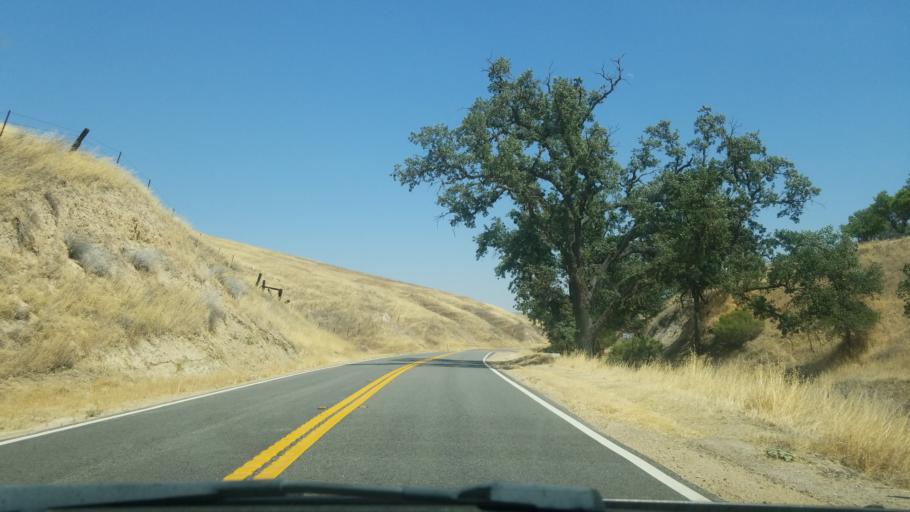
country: US
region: California
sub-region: San Luis Obispo County
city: Shandon
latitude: 35.5801
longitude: -120.4547
